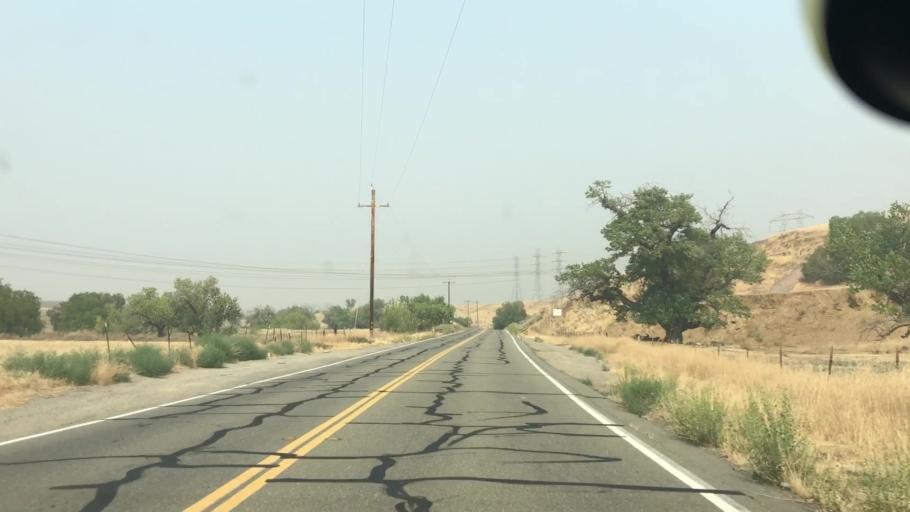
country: US
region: California
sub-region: San Joaquin County
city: Tracy
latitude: 37.6578
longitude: -121.4775
